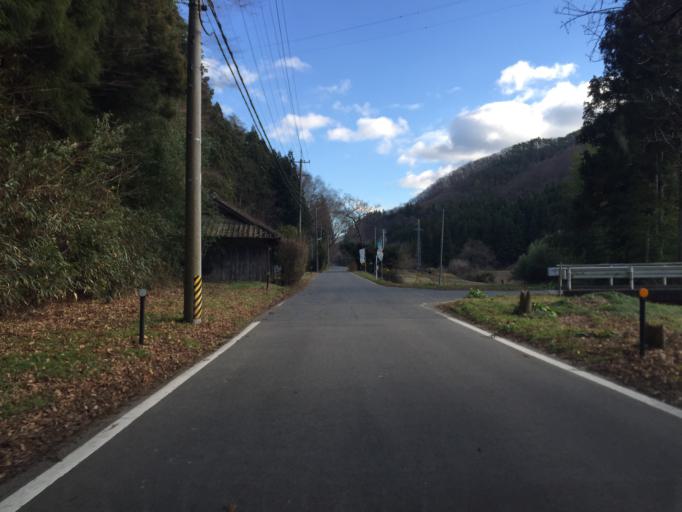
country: JP
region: Fukushima
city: Funehikimachi-funehiki
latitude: 37.2343
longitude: 140.6979
